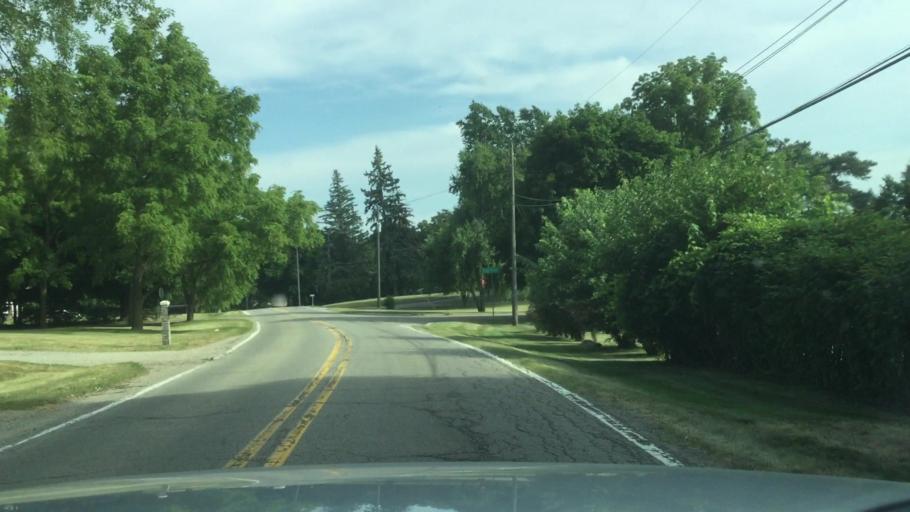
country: US
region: Michigan
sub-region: Oakland County
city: Sylvan Lake
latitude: 42.6384
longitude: -83.3422
